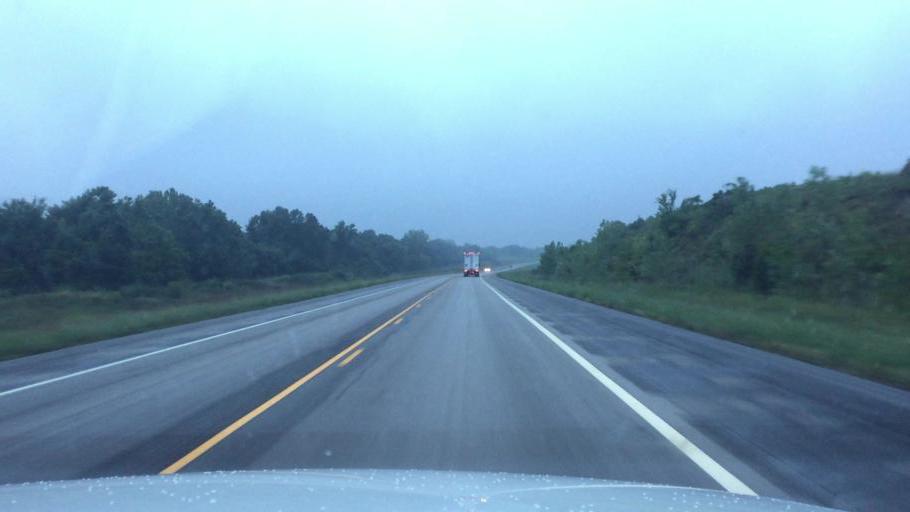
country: US
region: Kansas
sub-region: Montgomery County
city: Cherryvale
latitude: 37.4495
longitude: -95.4833
